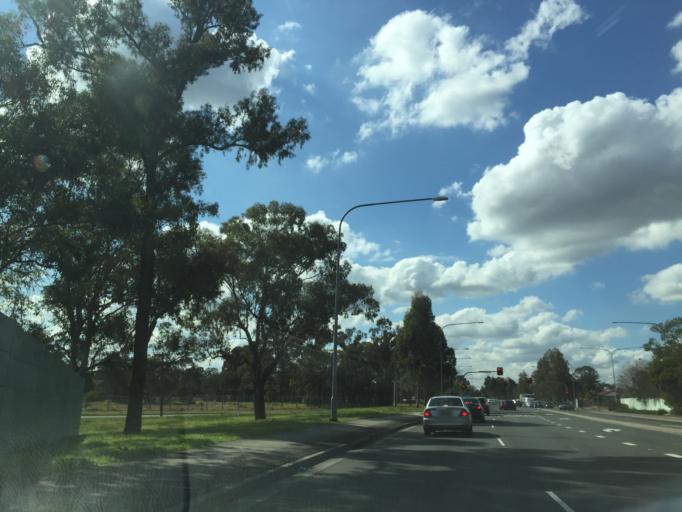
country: AU
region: New South Wales
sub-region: Blacktown
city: Quakers Hill
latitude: -33.7316
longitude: 150.8764
